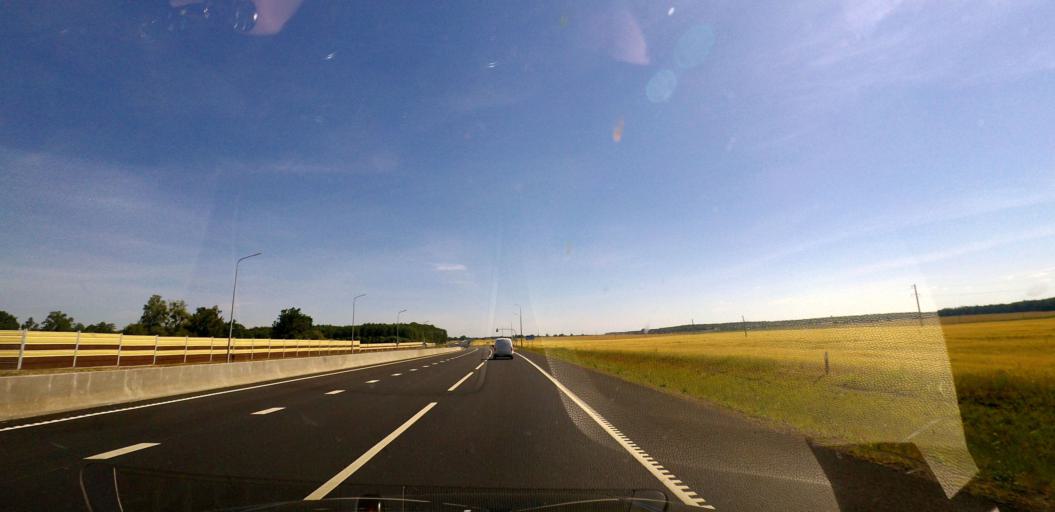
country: BY
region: Grodnenskaya
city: Shchuchin
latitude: 53.7156
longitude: 24.9539
